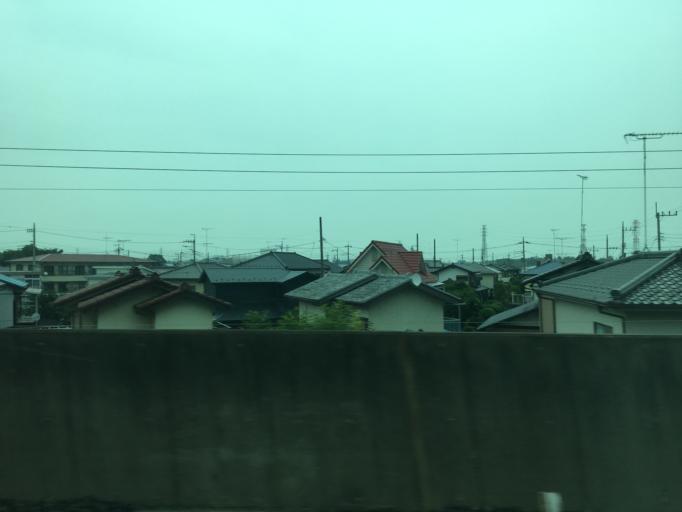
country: JP
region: Ibaraki
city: Koga
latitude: 36.1863
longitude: 139.7120
